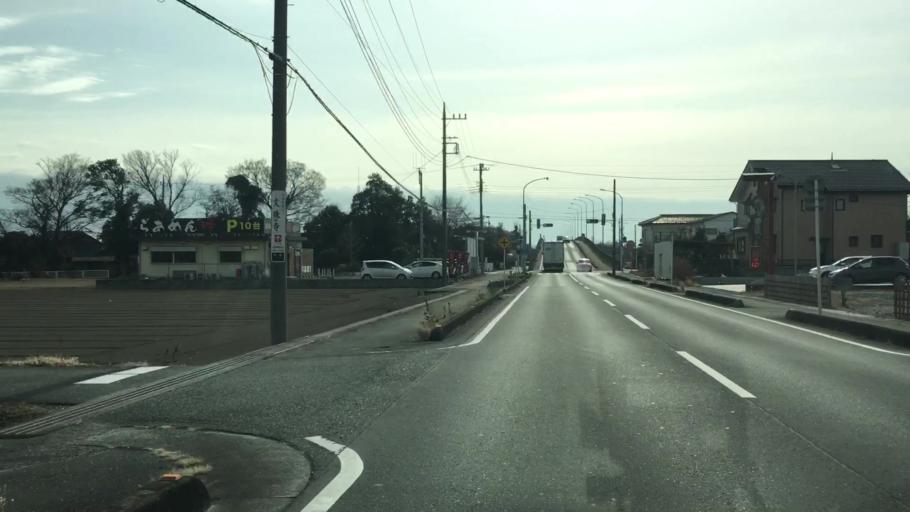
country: JP
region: Saitama
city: Fukayacho
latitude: 36.1472
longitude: 139.3227
